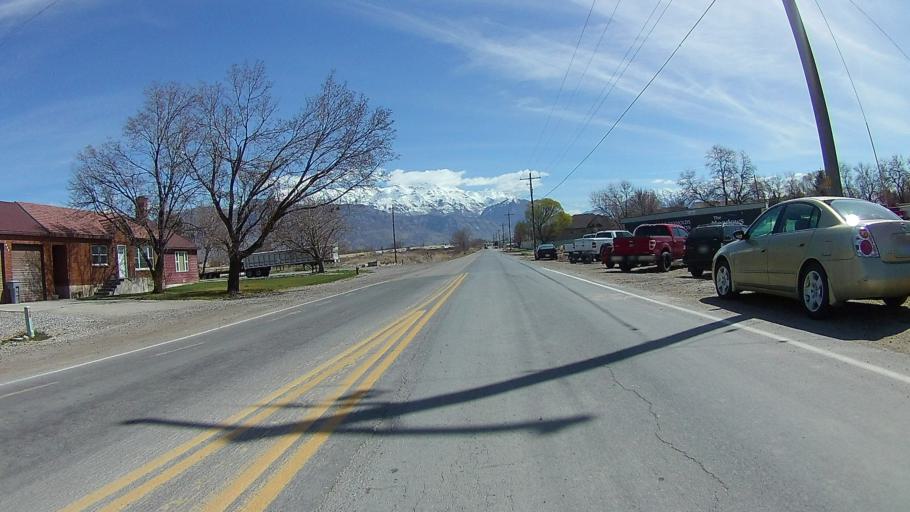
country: US
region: Utah
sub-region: Utah County
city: American Fork
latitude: 40.3728
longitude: -111.8187
